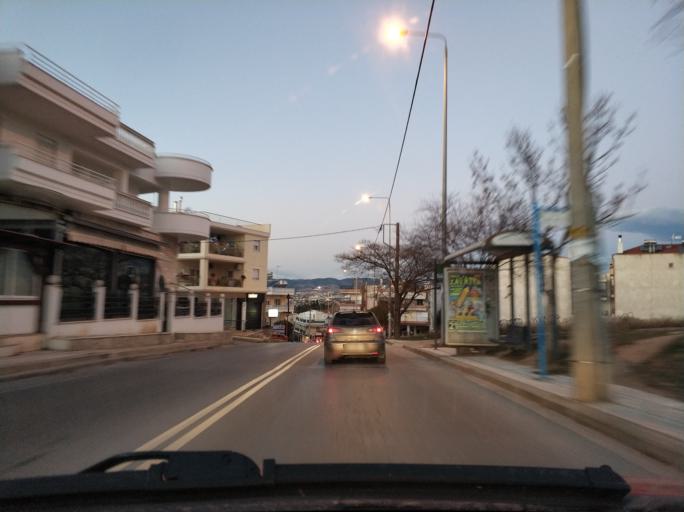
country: GR
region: Central Macedonia
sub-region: Nomos Thessalonikis
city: Polichni
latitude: 40.6689
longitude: 22.9458
